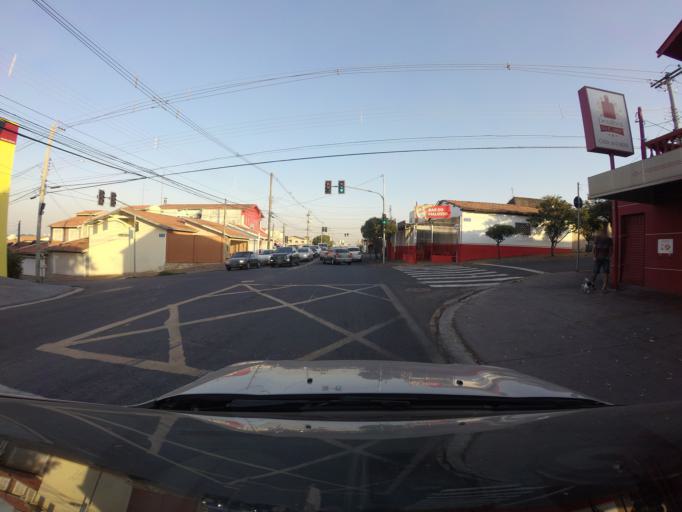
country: BR
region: Sao Paulo
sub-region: Piracicaba
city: Piracicaba
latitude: -22.7455
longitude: -47.6213
